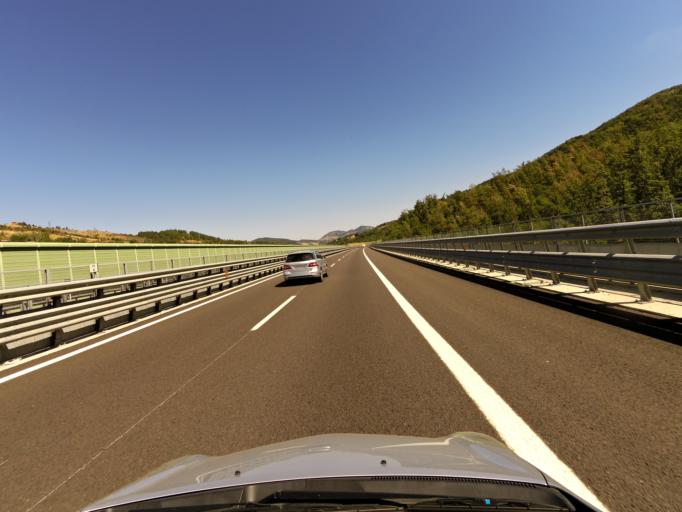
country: IT
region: Emilia-Romagna
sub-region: Provincia di Bologna
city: Grizzana
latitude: 44.2339
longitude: 11.1847
